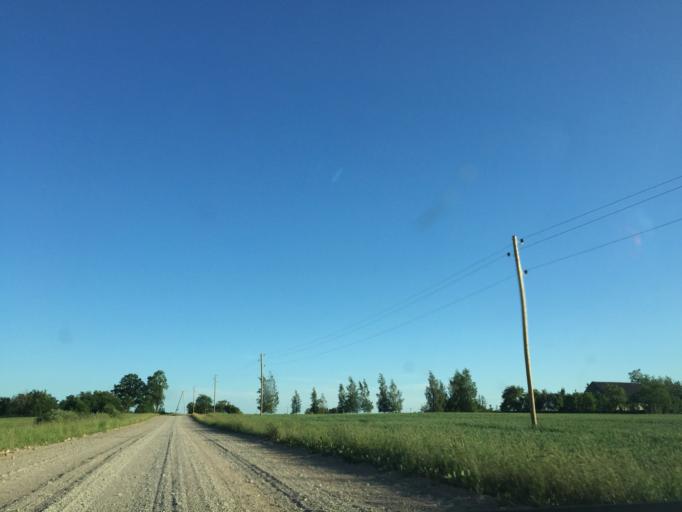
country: LV
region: Broceni
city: Broceni
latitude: 56.8068
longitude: 22.5477
